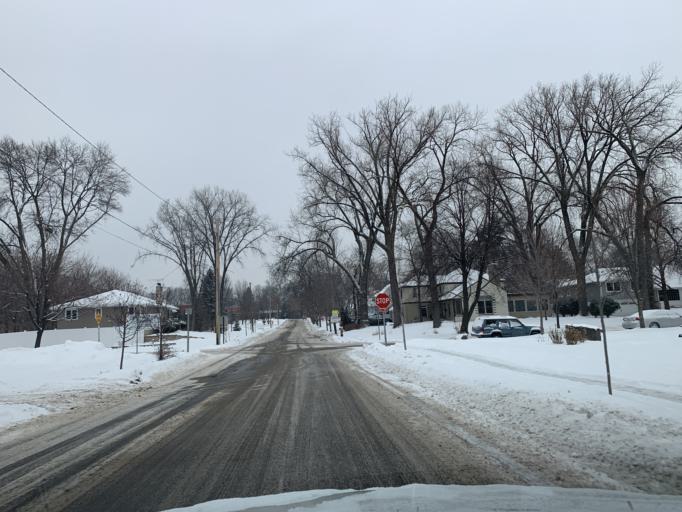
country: US
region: Minnesota
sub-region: Hennepin County
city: Saint Louis Park
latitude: 44.9494
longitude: -93.3339
